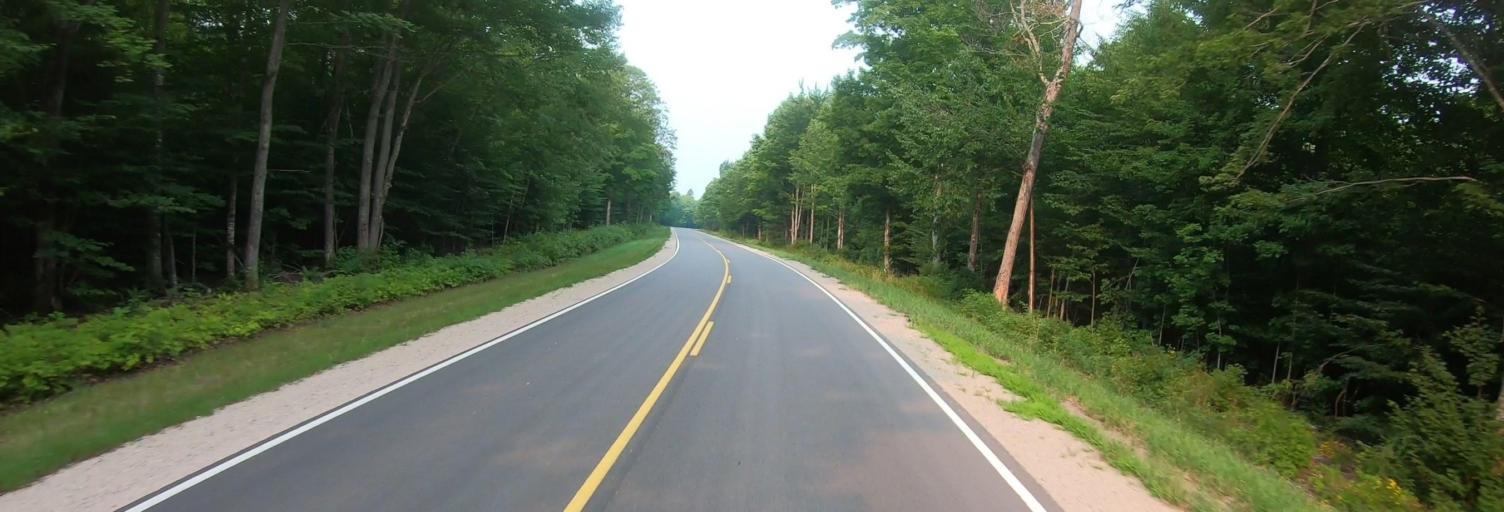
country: US
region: Michigan
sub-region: Luce County
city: Newberry
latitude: 46.4869
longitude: -85.0889
